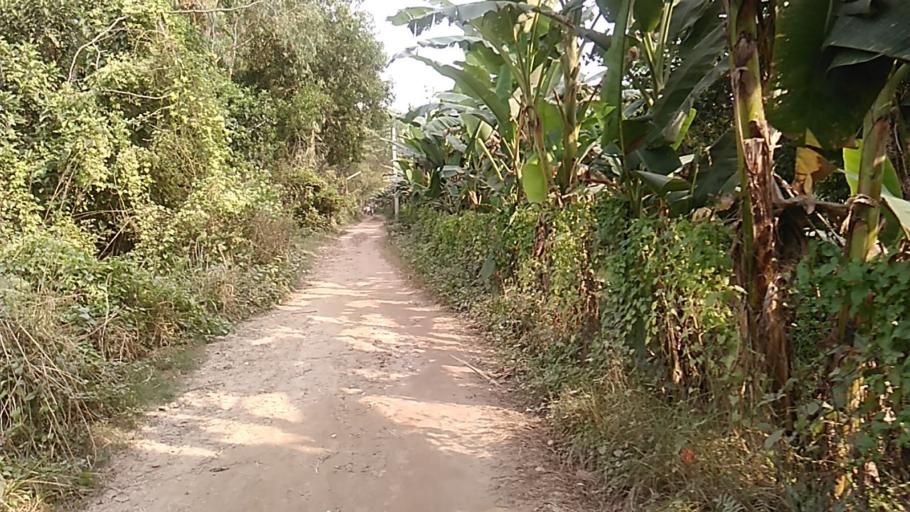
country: IN
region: West Bengal
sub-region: Nadia
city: Navadwip
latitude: 23.4259
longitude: 88.3957
